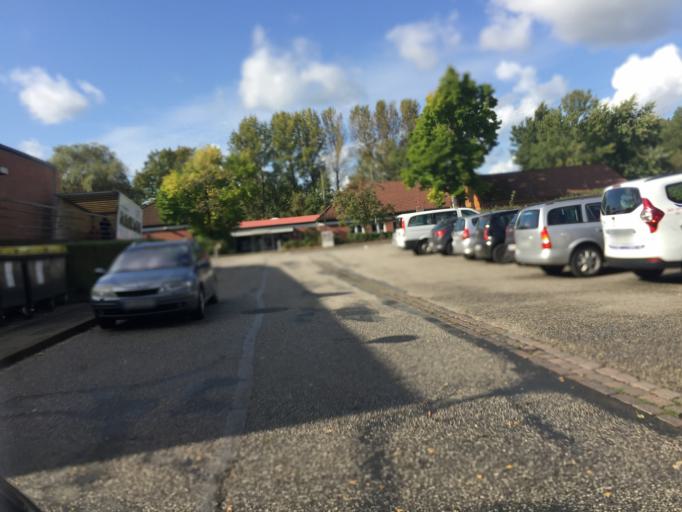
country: DE
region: Schleswig-Holstein
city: Heiligenstedten
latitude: 53.9369
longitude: 9.4928
